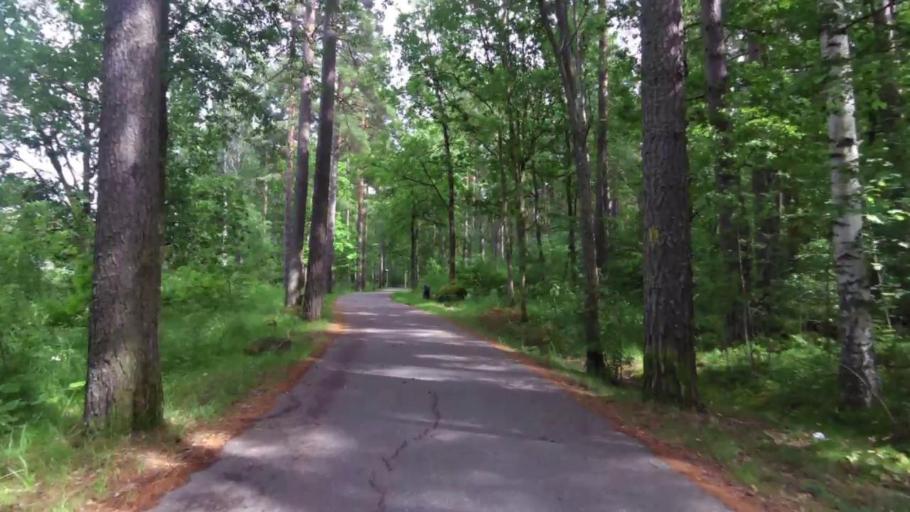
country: SE
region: OEstergoetland
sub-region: Linkopings Kommun
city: Linkoping
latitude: 58.4125
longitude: 15.5804
